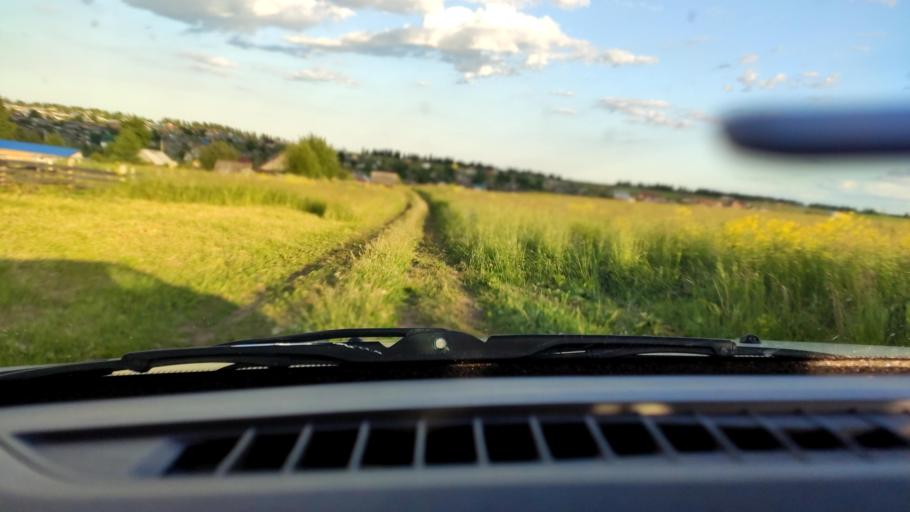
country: RU
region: Perm
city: Uinskoye
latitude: 57.1150
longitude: 56.5024
